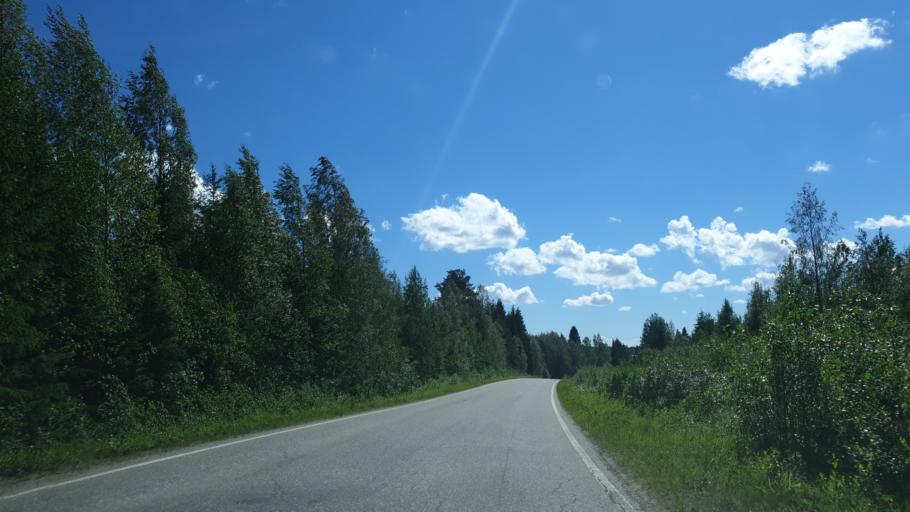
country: FI
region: Northern Savo
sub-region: Koillis-Savo
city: Kaavi
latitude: 62.9890
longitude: 28.5049
